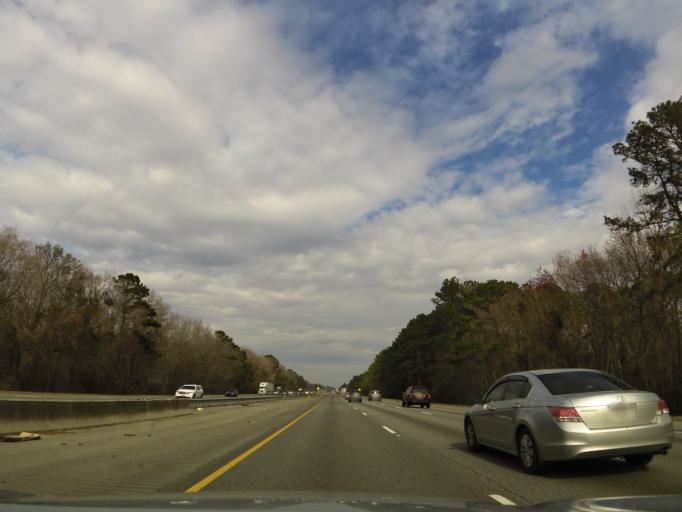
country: US
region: Georgia
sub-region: Bryan County
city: Richmond Hill
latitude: 31.9740
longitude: -81.3147
